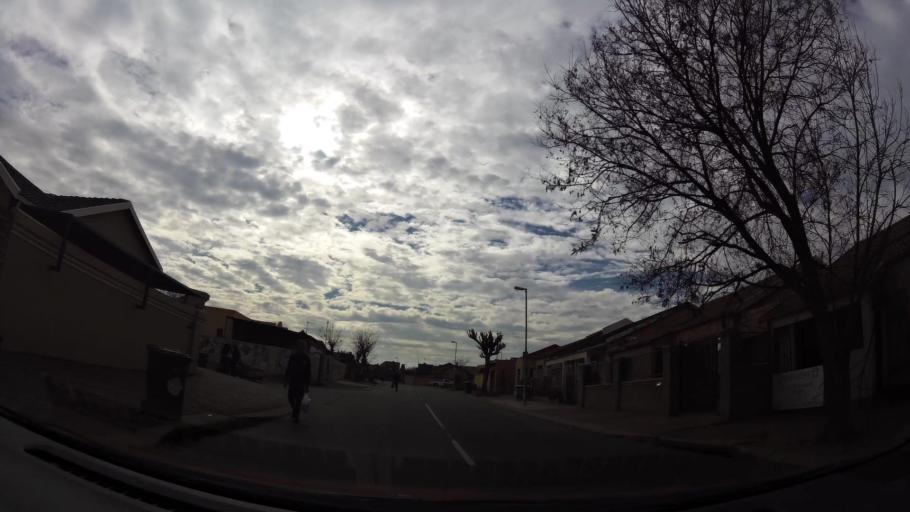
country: ZA
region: Gauteng
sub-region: City of Johannesburg Metropolitan Municipality
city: Soweto
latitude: -26.2745
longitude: 27.8333
